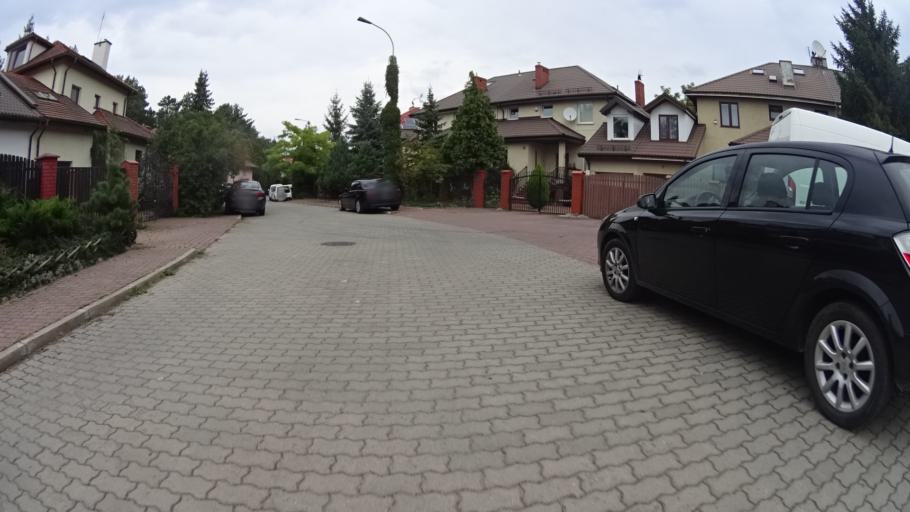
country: PL
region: Masovian Voivodeship
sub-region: Powiat pruszkowski
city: Nadarzyn
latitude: 52.1054
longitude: 20.7980
